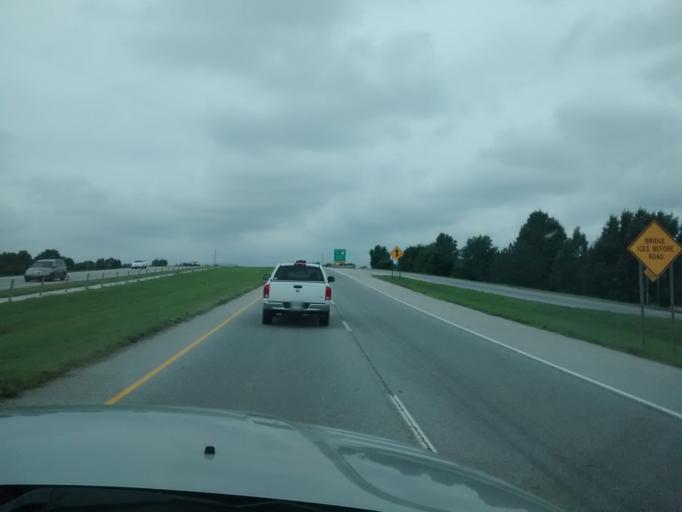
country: US
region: Arkansas
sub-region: Washington County
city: Johnson
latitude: 36.1125
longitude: -94.1605
